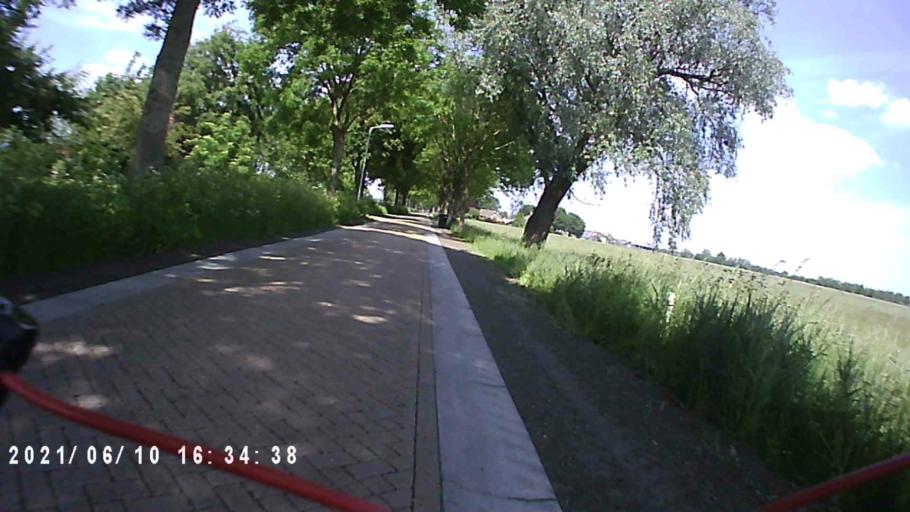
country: NL
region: Friesland
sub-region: Gemeente Achtkarspelen
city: Buitenpost
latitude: 53.2320
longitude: 6.1322
